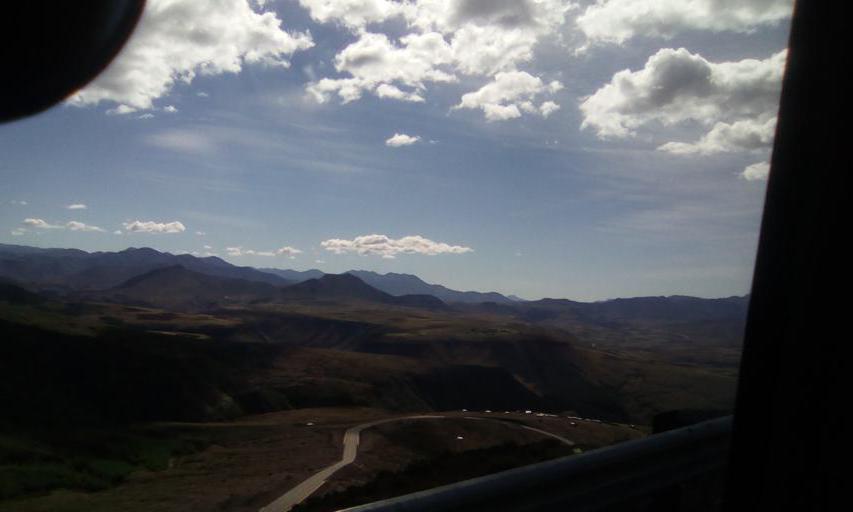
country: LS
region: Qacha's Nek
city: Qacha's Nek
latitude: -30.0104
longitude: 28.1682
